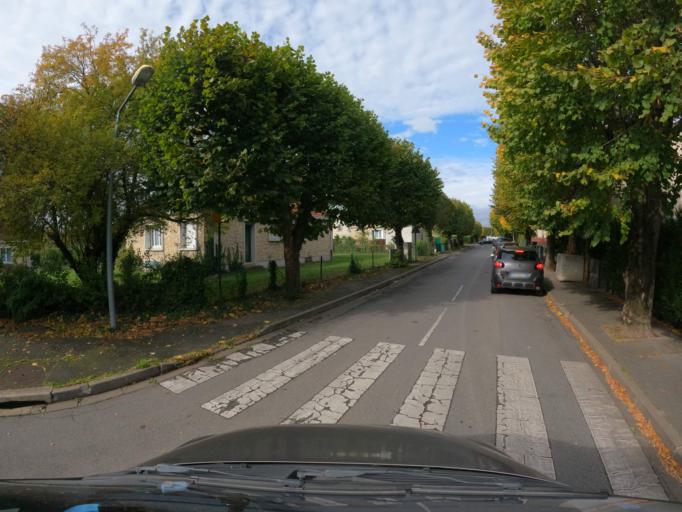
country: FR
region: Ile-de-France
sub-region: Departement de Seine-et-Marne
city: Brou-sur-Chantereine
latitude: 48.8831
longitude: 2.6219
